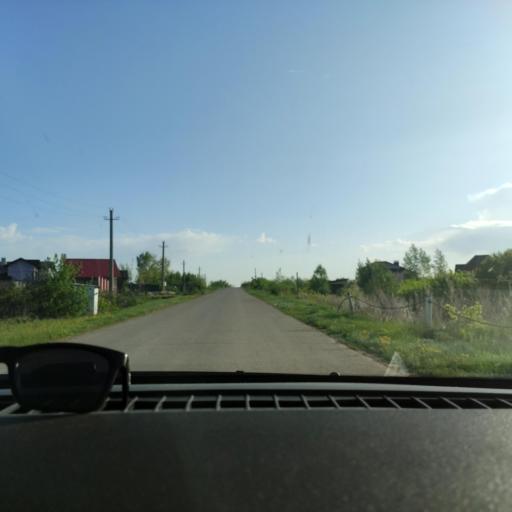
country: RU
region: Samara
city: Volzhskiy
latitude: 53.4410
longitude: 50.1842
